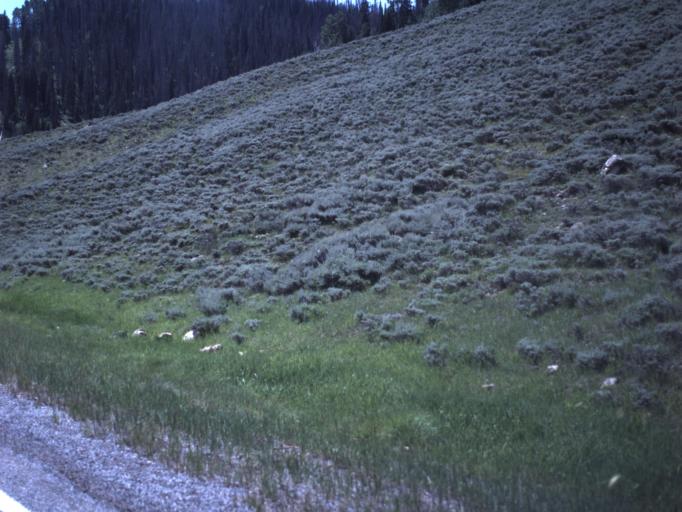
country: US
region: Utah
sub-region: Sanpete County
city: Fairview
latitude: 39.6755
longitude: -111.2439
